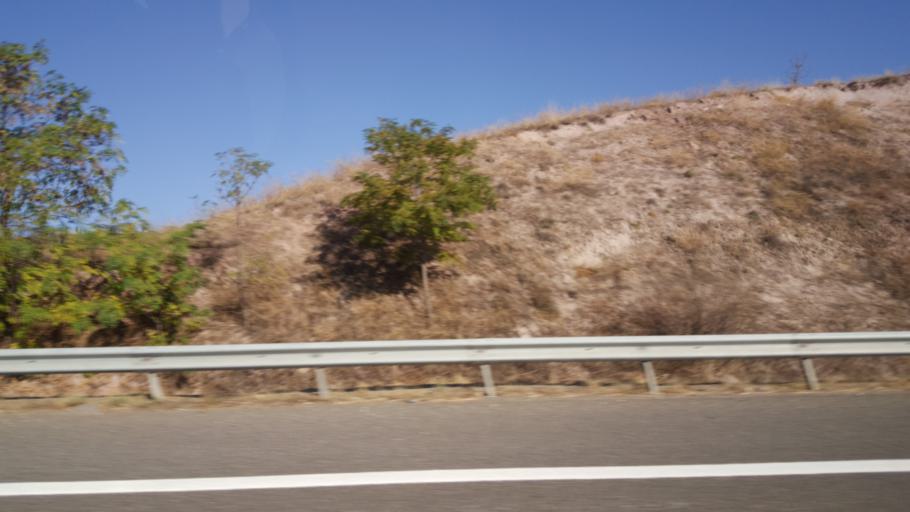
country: TR
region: Ankara
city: Mamak
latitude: 40.0161
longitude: 32.9241
